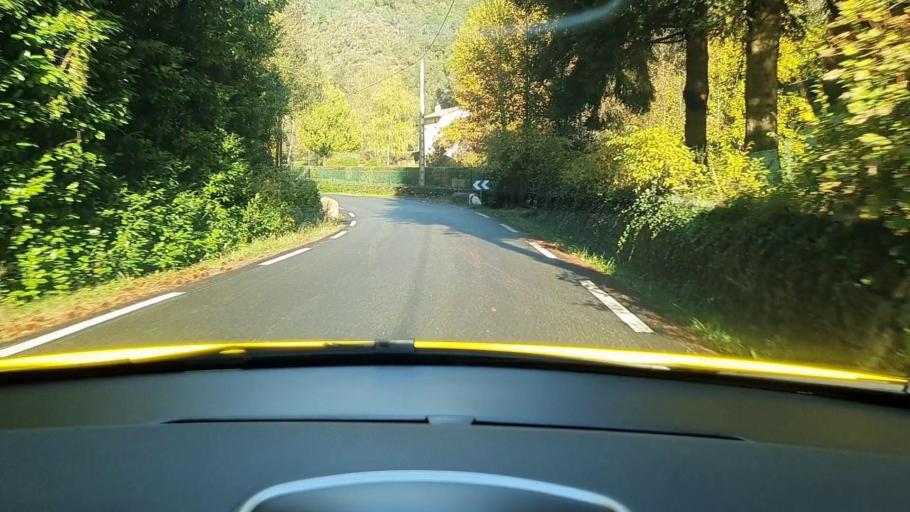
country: FR
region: Languedoc-Roussillon
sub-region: Departement du Gard
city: Lasalle
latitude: 44.1280
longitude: 3.7628
